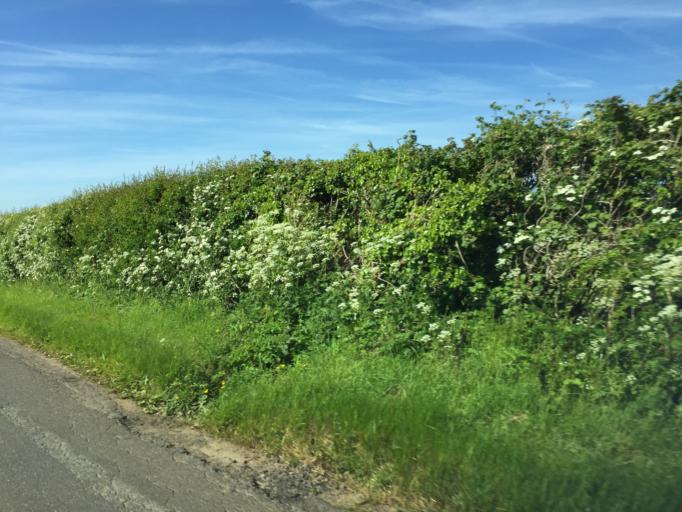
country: GB
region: England
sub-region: South Gloucestershire
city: Horton
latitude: 51.5313
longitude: -2.3091
